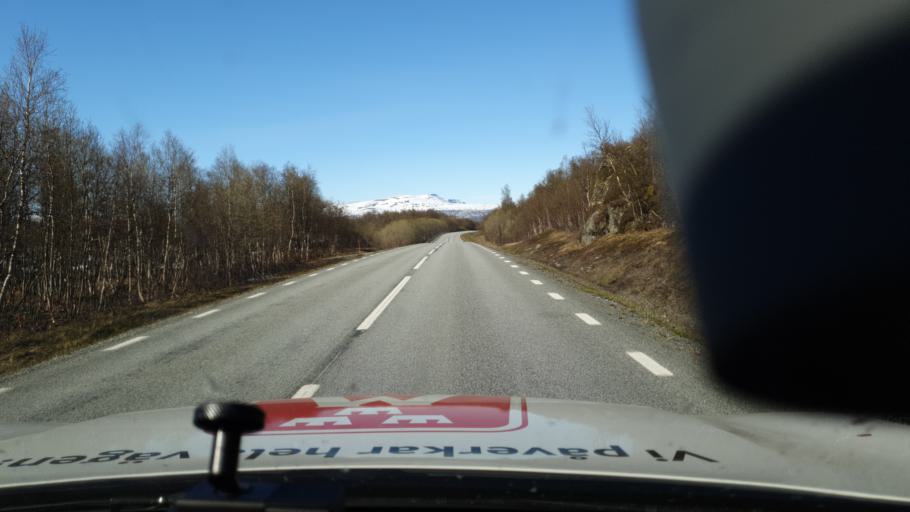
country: NO
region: Nordland
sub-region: Rana
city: Mo i Rana
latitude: 65.9598
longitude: 15.0345
